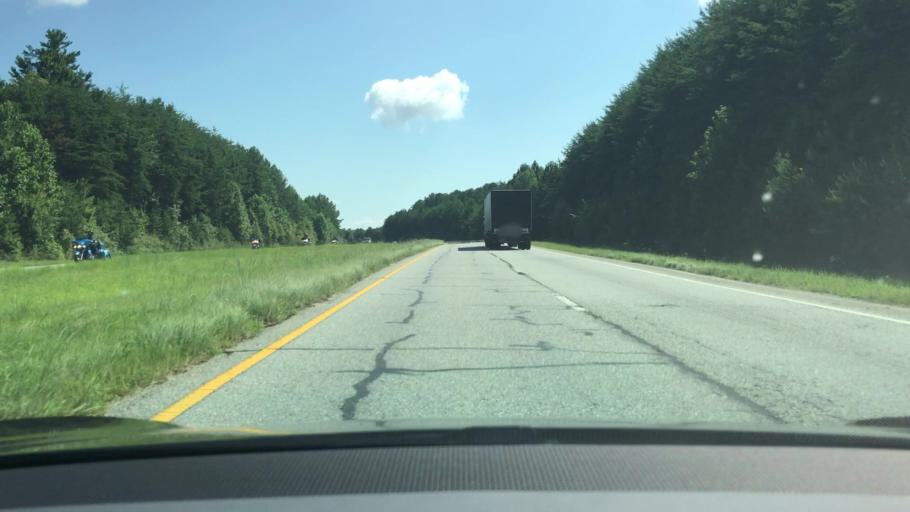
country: US
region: Georgia
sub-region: Habersham County
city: Clarkesville
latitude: 34.6996
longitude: -83.4165
